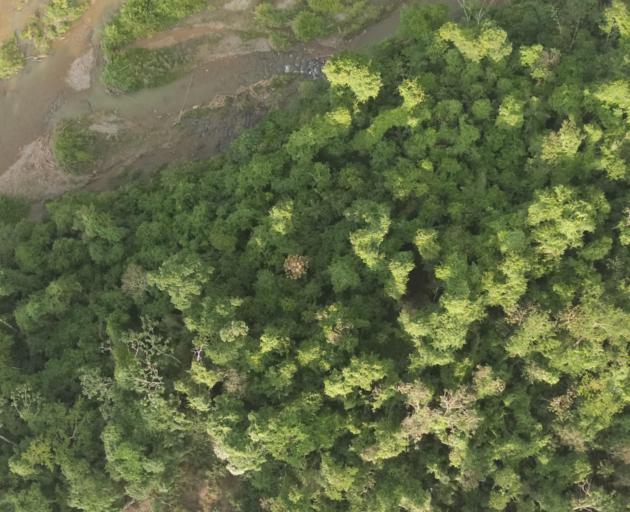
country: BO
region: La Paz
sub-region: Provincia Larecaja
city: Guanay
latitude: -15.7727
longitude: -67.6608
